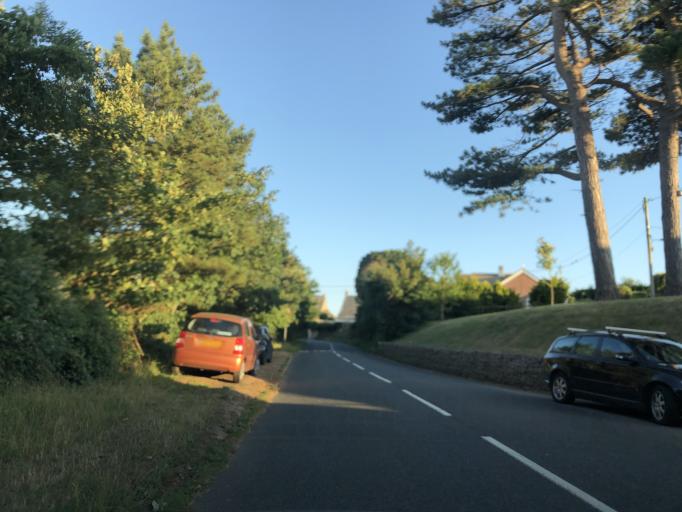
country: GB
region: England
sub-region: Isle of Wight
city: Chale
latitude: 50.6110
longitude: -1.3200
